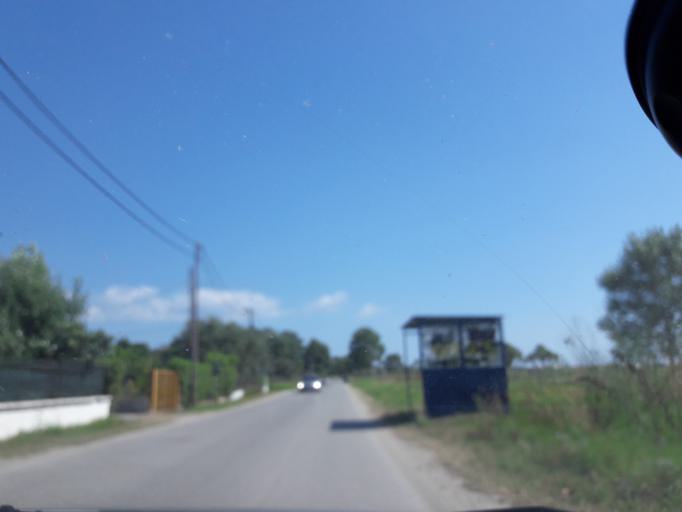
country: GR
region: Central Macedonia
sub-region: Nomos Chalkidikis
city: Nea Kallikrateia
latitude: 40.3384
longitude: 23.0191
